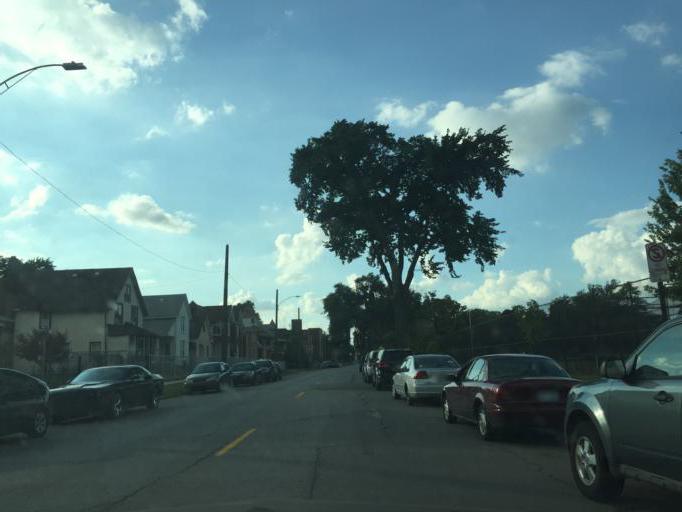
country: US
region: Michigan
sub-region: Wayne County
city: Detroit
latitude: 42.3144
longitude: -83.0916
